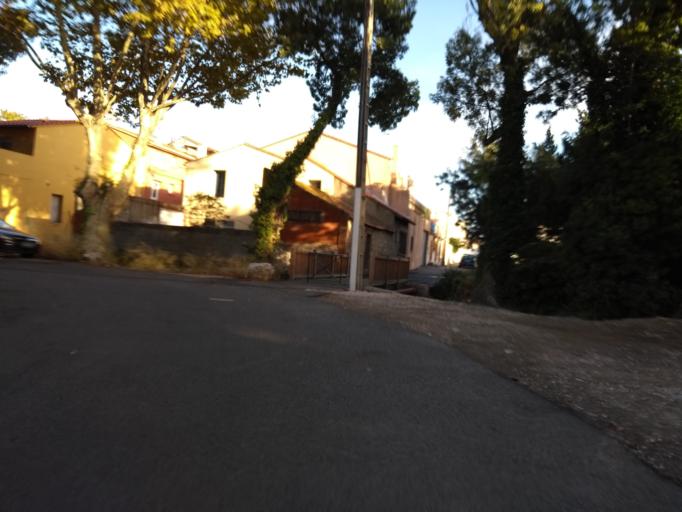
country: FR
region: Languedoc-Roussillon
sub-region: Departement des Pyrenees-Orientales
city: Perpignan
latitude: 42.7198
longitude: 2.8874
